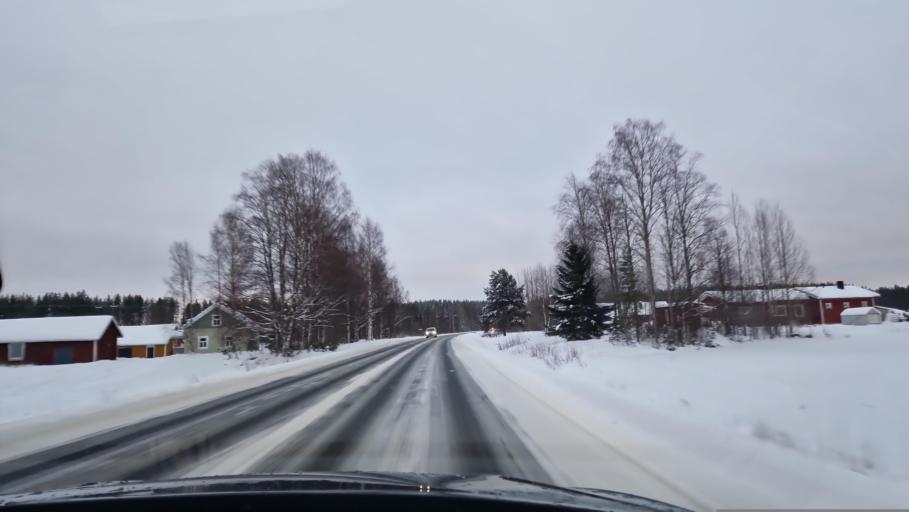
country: FI
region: North Karelia
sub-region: Pielisen Karjala
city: Valtimo
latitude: 64.0871
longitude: 28.8708
